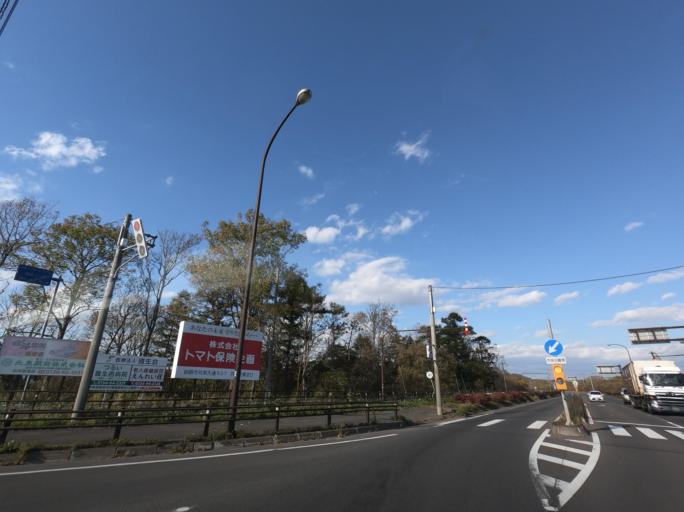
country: JP
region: Hokkaido
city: Kushiro
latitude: 43.0544
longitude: 144.2949
